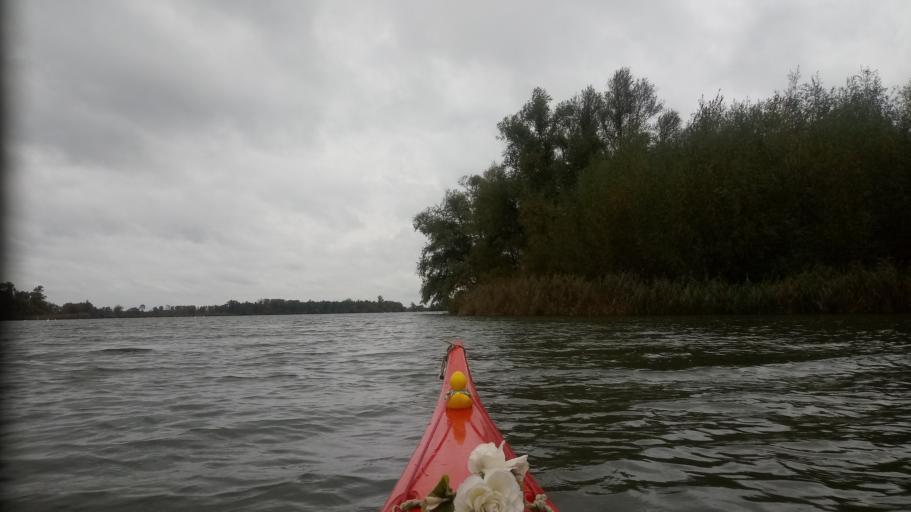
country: NL
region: North Brabant
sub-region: Gemeente Made en Drimmelen
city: Drimmelen
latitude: 51.7481
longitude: 4.7801
